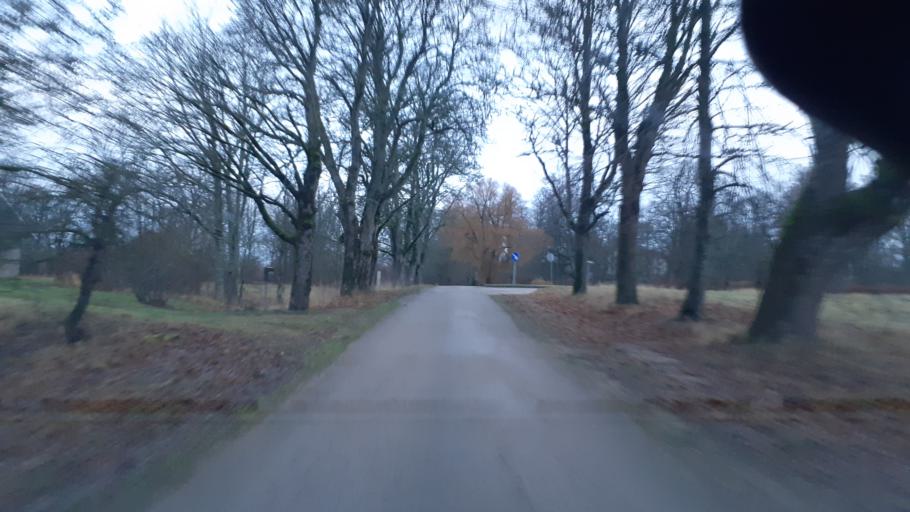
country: LV
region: Alsunga
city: Alsunga
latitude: 56.9023
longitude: 21.6968
